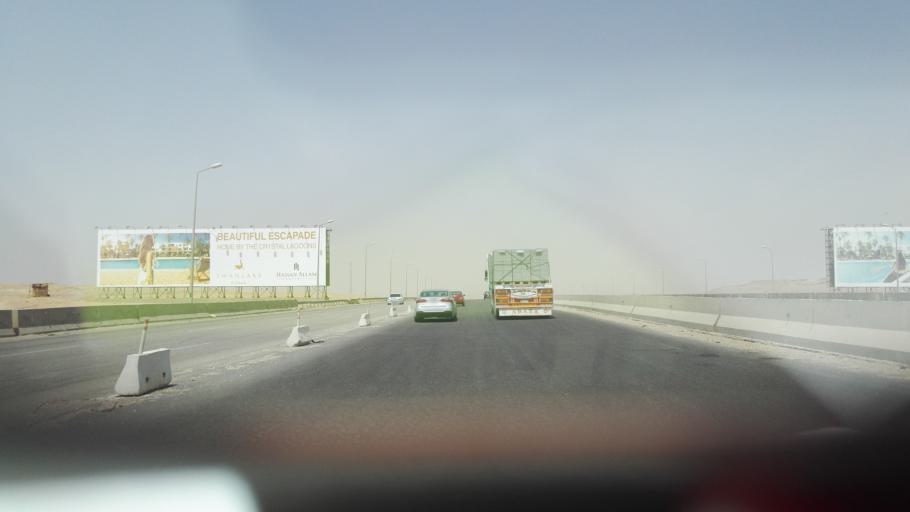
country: EG
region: As Suways
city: Ain Sukhna
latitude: 29.7213
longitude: 32.0568
